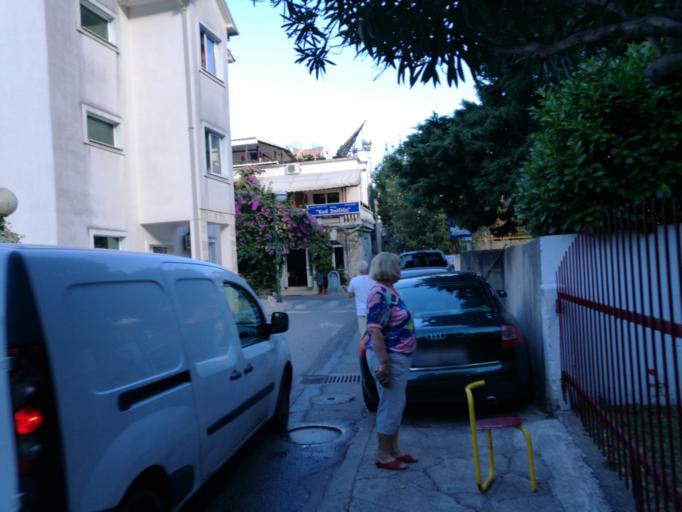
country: ME
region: Budva
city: Budva
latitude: 42.2801
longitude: 18.8822
